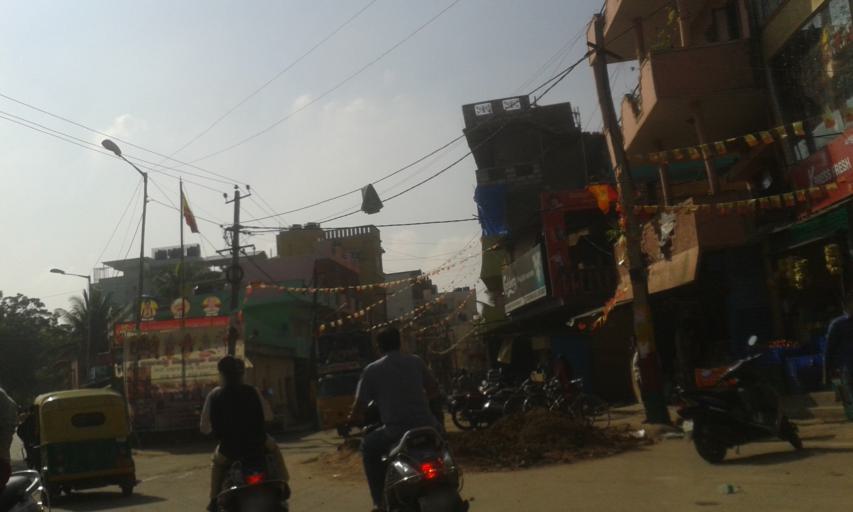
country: IN
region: Karnataka
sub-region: Bangalore Urban
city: Bangalore
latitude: 12.9466
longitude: 77.6289
